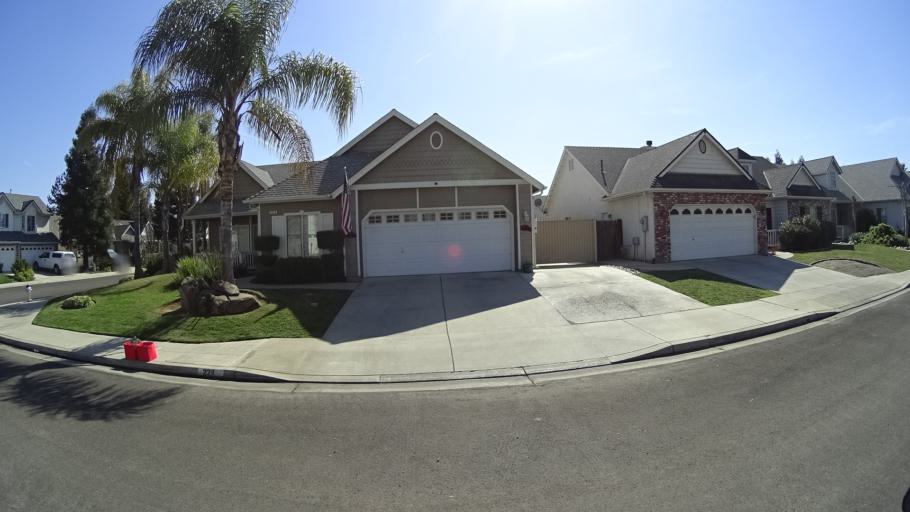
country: US
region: California
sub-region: Fresno County
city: Clovis
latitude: 36.8845
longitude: -119.7438
